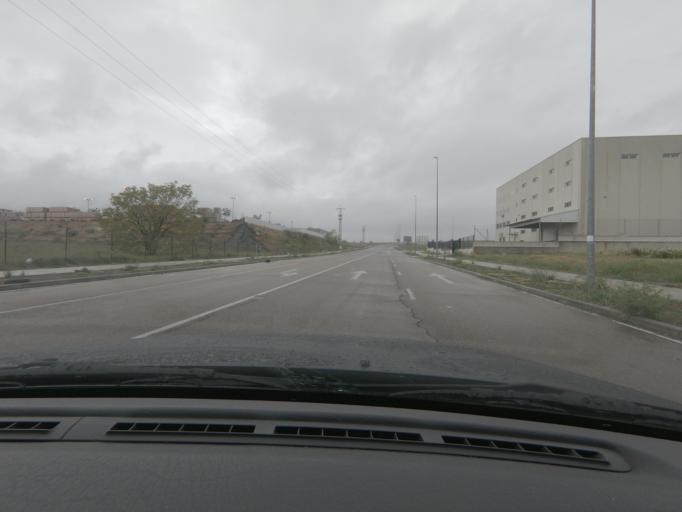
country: ES
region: Extremadura
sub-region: Provincia de Badajoz
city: Badajoz
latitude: 38.9007
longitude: -6.9968
